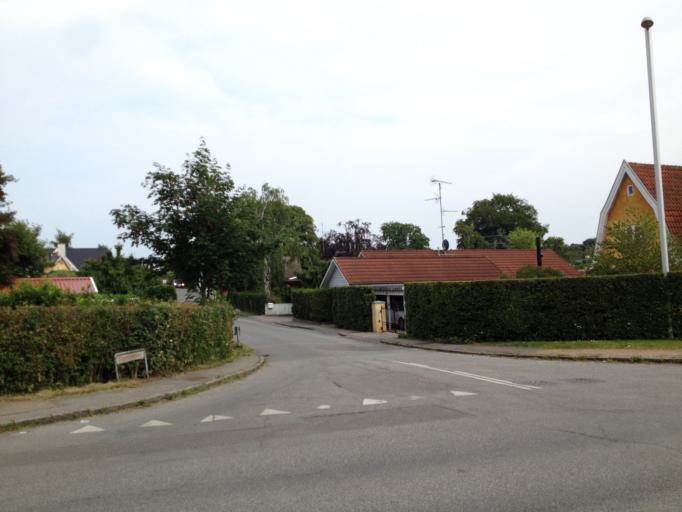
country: DK
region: Capital Region
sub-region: Fredensborg Kommune
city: Humlebaek
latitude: 55.9531
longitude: 12.5269
